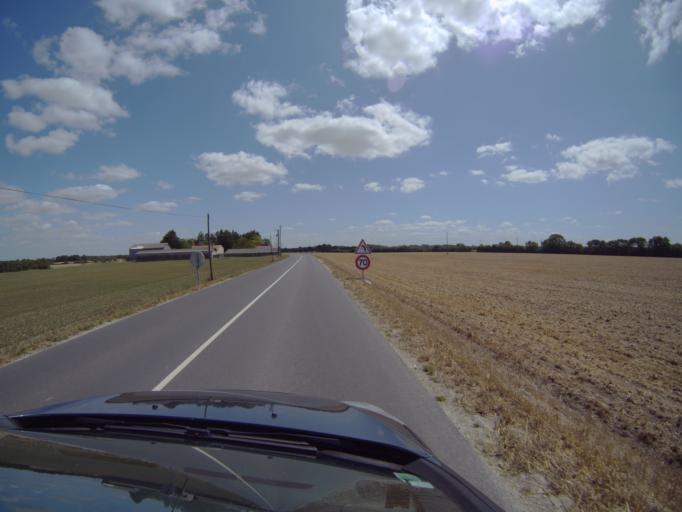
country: FR
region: Poitou-Charentes
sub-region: Departement de la Charente-Maritime
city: Saint-Jean-de-Liversay
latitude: 46.2770
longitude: -0.9123
